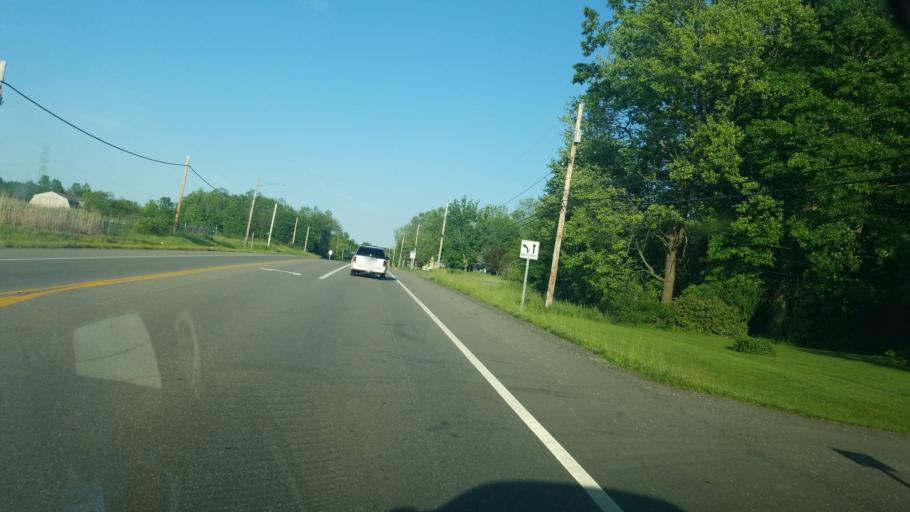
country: US
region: Ohio
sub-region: Portage County
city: Ravenna
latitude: 41.1568
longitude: -81.2154
